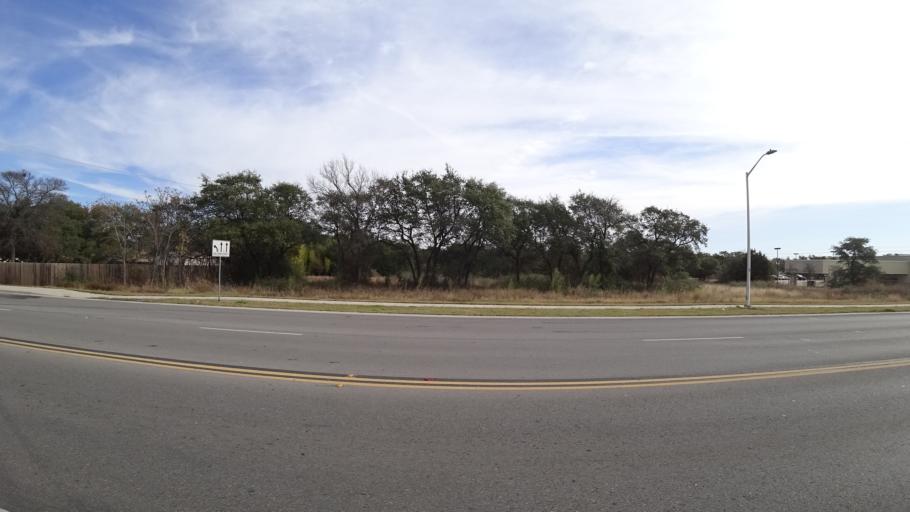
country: US
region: Texas
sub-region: Williamson County
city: Cedar Park
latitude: 30.5191
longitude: -97.8407
